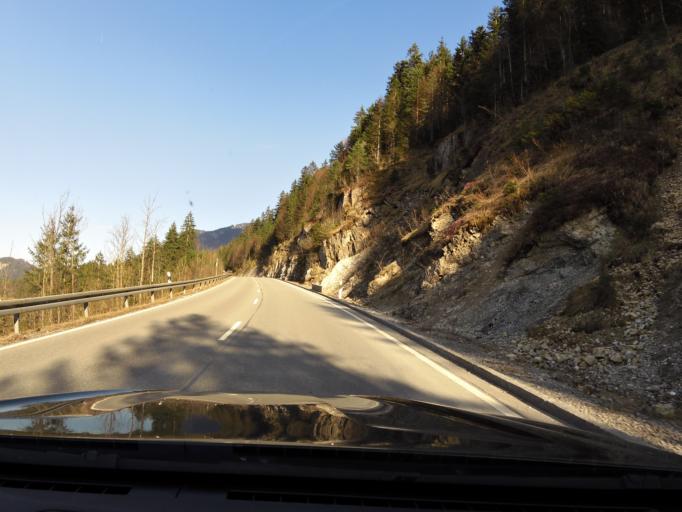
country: DE
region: Bavaria
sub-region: Upper Bavaria
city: Jachenau
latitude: 47.5603
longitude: 11.5043
